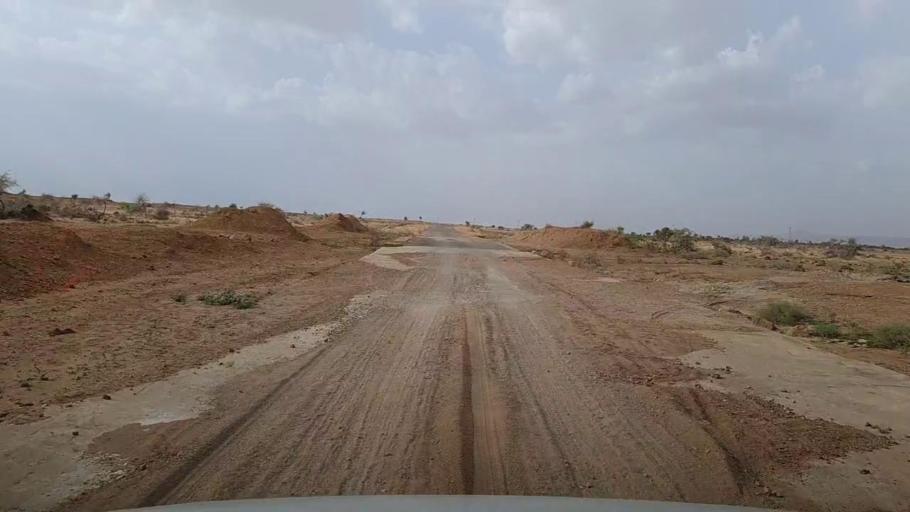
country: PK
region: Sindh
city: Jamshoro
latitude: 25.4627
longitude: 67.6773
